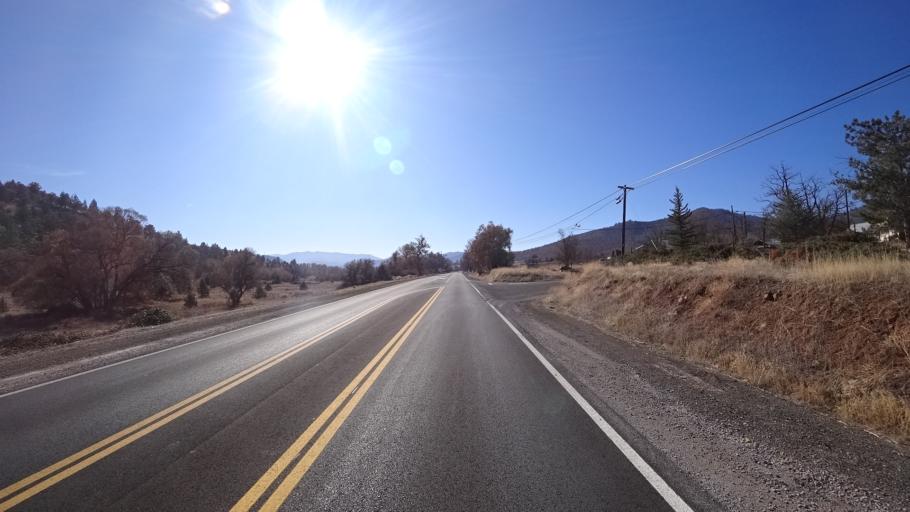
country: US
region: California
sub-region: Siskiyou County
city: Yreka
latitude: 41.7614
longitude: -122.6216
